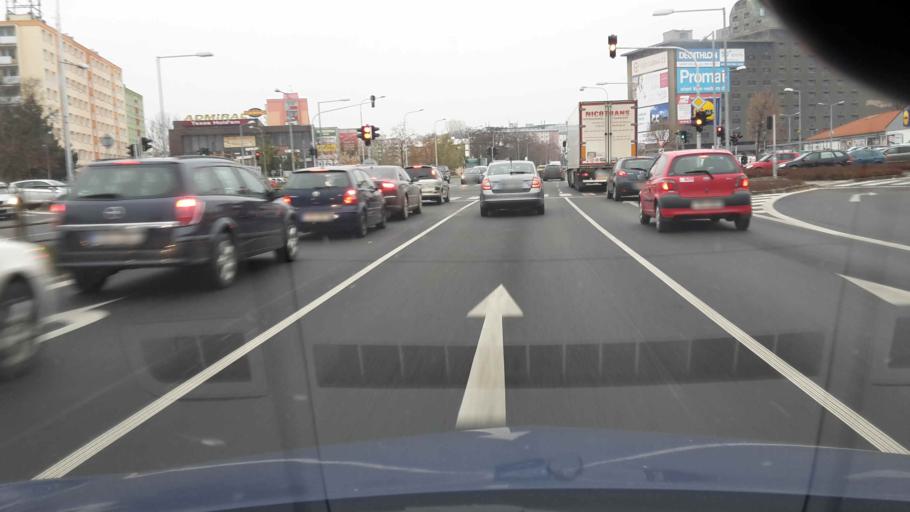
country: CZ
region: Olomoucky
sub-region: Okres Olomouc
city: Olomouc
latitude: 49.5813
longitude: 17.2499
